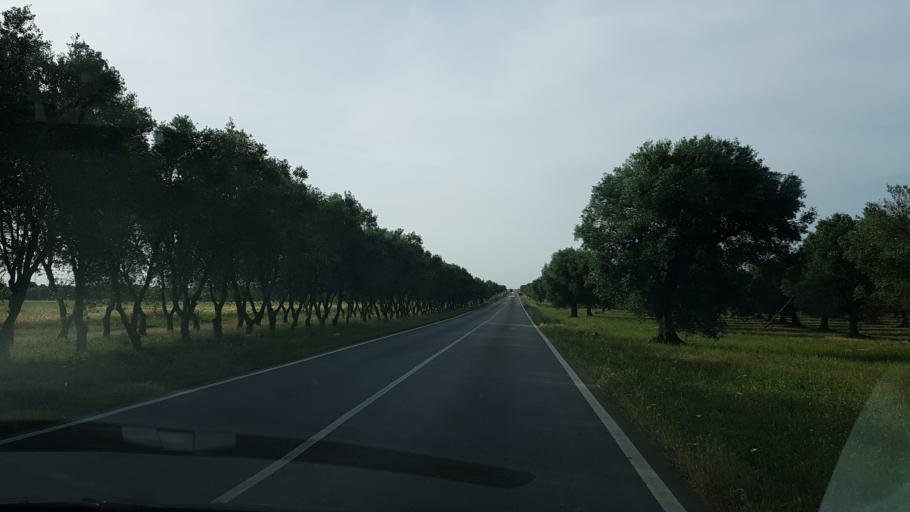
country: IT
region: Apulia
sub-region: Provincia di Brindisi
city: San Pancrazio Salentino
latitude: 40.3693
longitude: 17.8399
